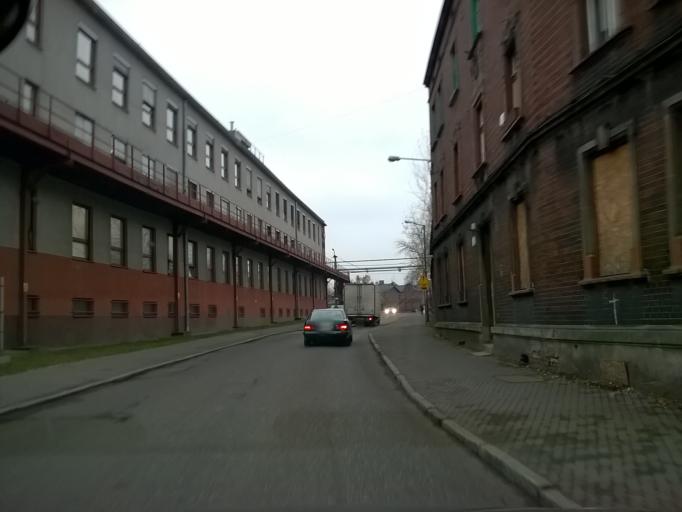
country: PL
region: Silesian Voivodeship
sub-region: Swietochlowice
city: Swietochlowice
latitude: 50.2763
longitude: 18.9433
